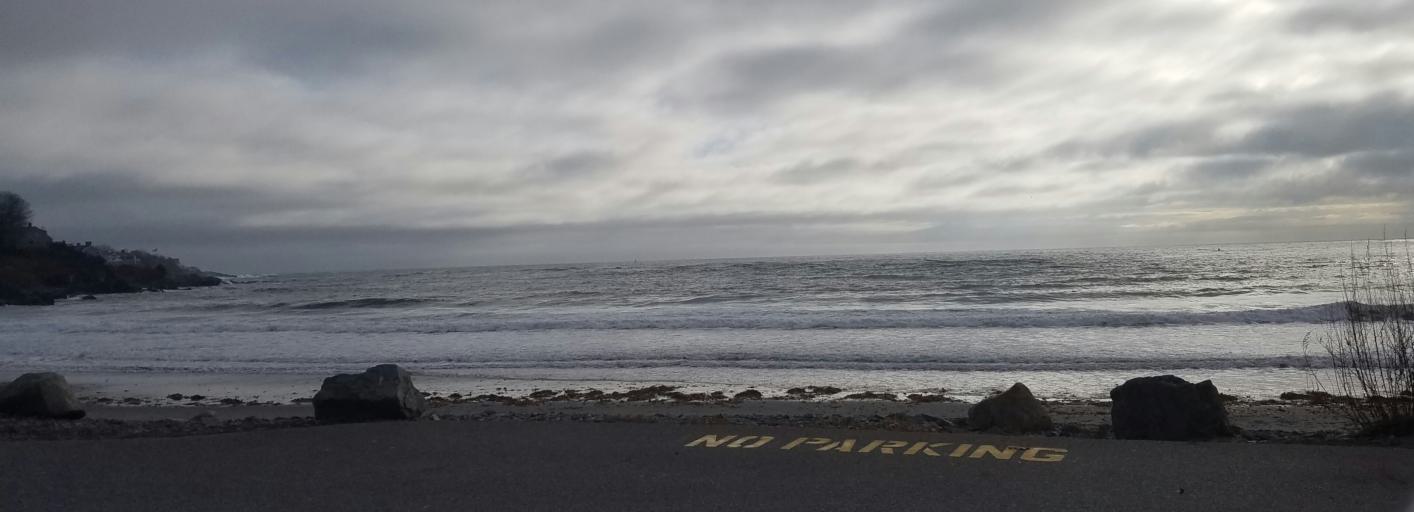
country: US
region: Maine
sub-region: York County
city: York Harbor
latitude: 43.1341
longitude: -70.6380
